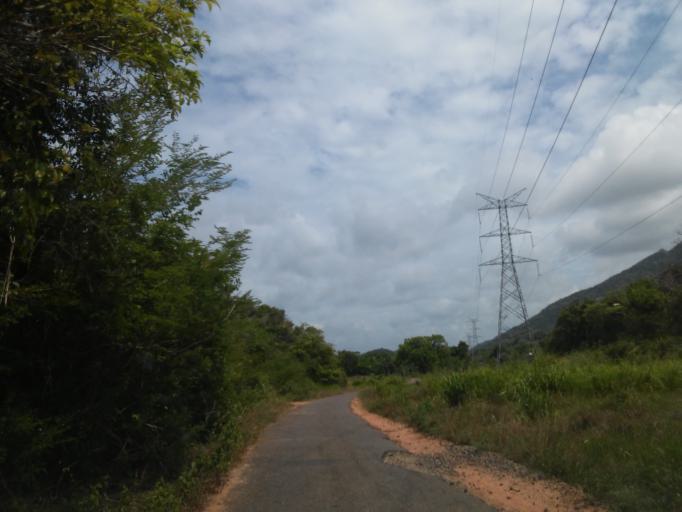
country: LK
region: Central
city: Sigiriya
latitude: 8.0879
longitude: 80.6793
